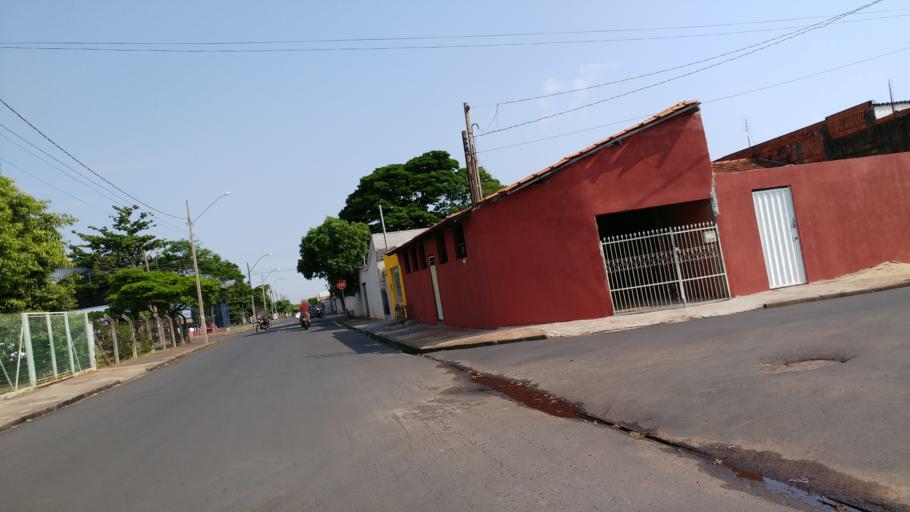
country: BR
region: Sao Paulo
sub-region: Paraguacu Paulista
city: Paraguacu Paulista
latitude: -22.4281
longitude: -50.5809
